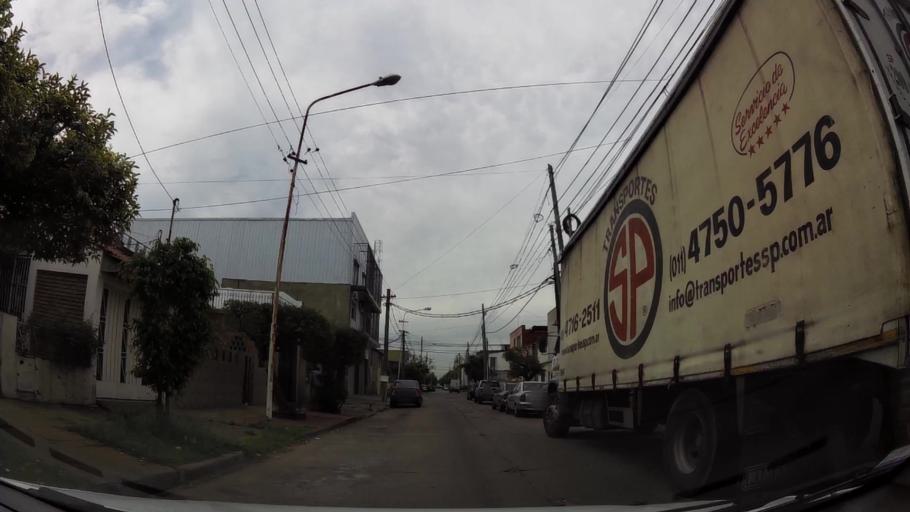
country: AR
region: Buenos Aires
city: San Justo
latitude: -34.6731
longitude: -58.5379
